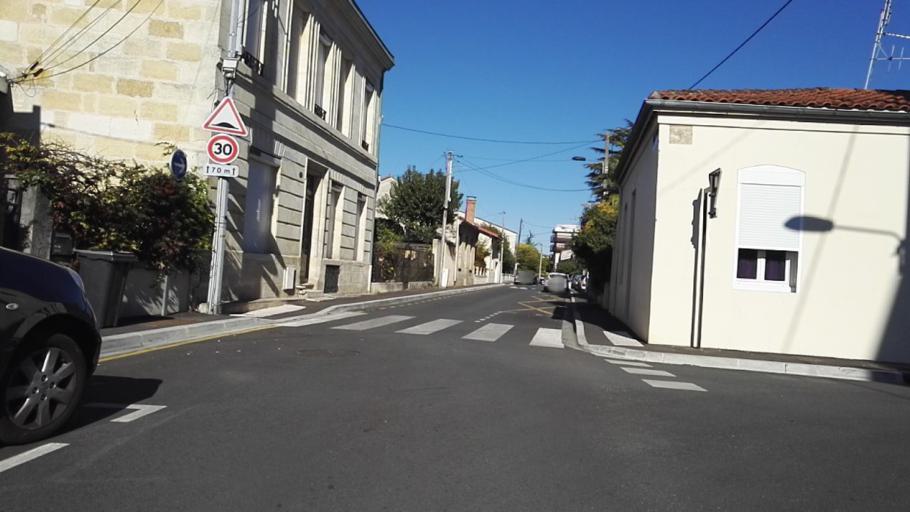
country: FR
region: Aquitaine
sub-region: Departement de la Gironde
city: Merignac
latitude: 44.8437
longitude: -0.6138
